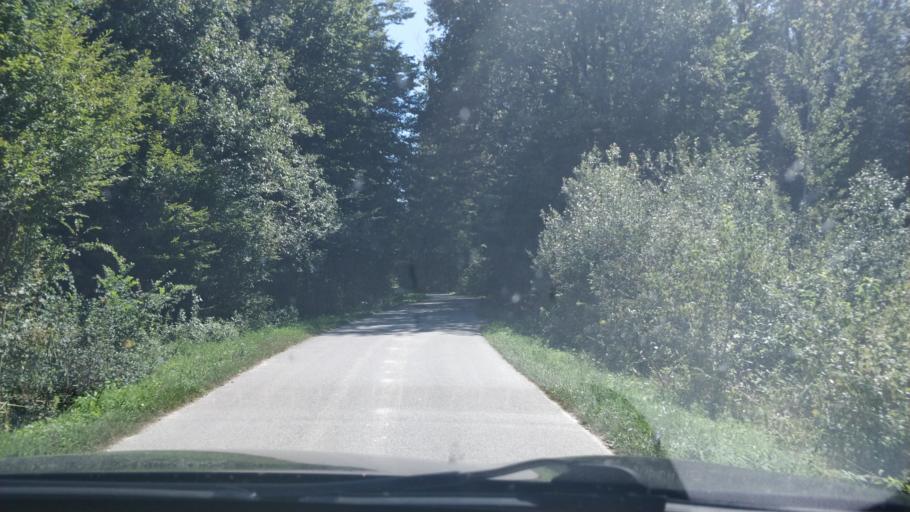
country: HR
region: Karlovacka
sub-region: Grad Karlovac
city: Karlovac
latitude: 45.4732
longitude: 15.6613
